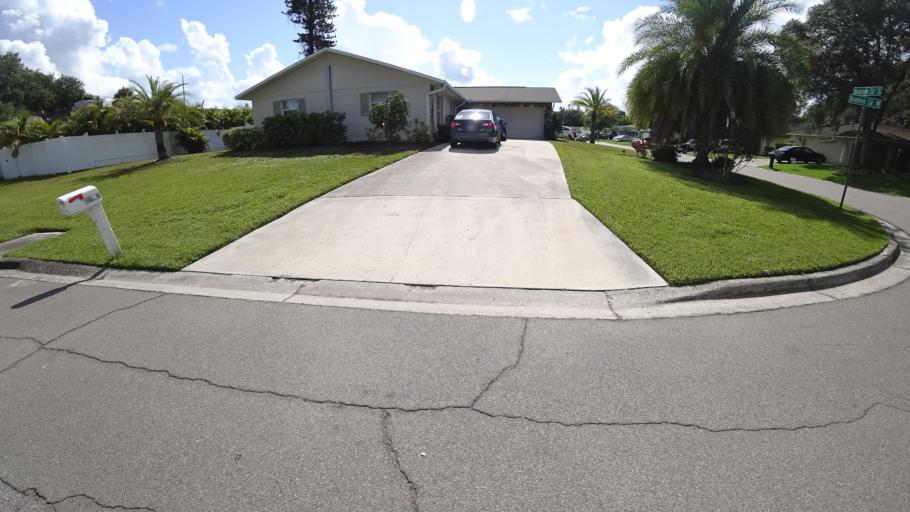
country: US
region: Florida
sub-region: Sarasota County
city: Desoto Lakes
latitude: 27.3893
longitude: -82.4985
